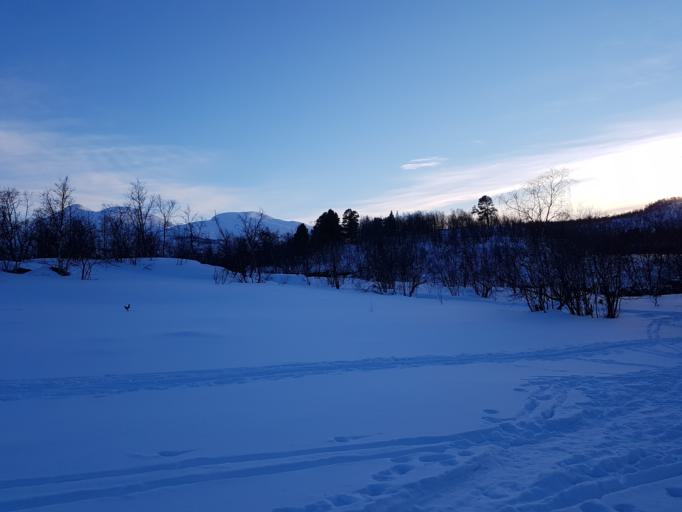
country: NO
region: Troms
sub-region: Bardu
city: Setermoen
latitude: 68.3424
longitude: 18.7648
